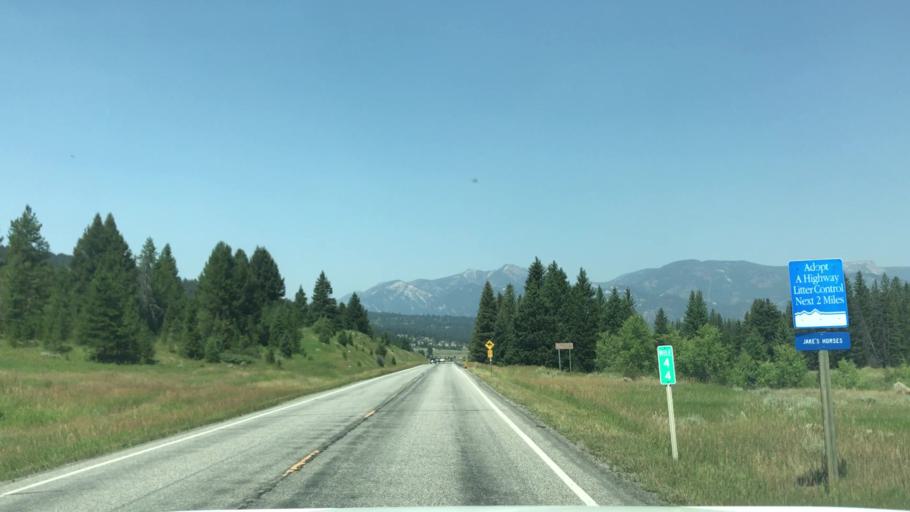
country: US
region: Montana
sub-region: Gallatin County
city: Big Sky
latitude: 45.2087
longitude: -111.2450
